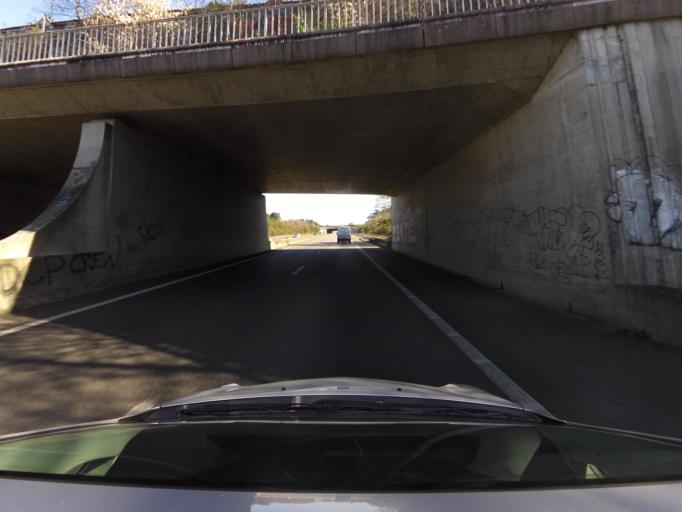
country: FR
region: Brittany
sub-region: Departement d'Ille-et-Vilaine
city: Fouillard
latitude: 48.1861
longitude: -1.5503
